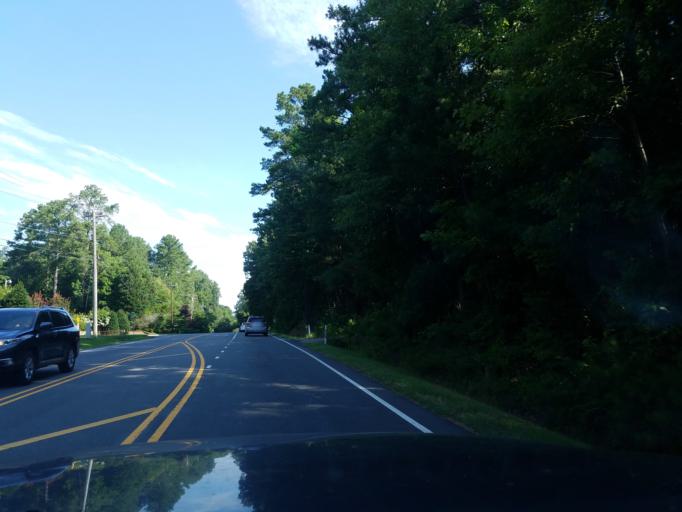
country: US
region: North Carolina
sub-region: Durham County
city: Durham
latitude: 35.9412
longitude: -78.9655
